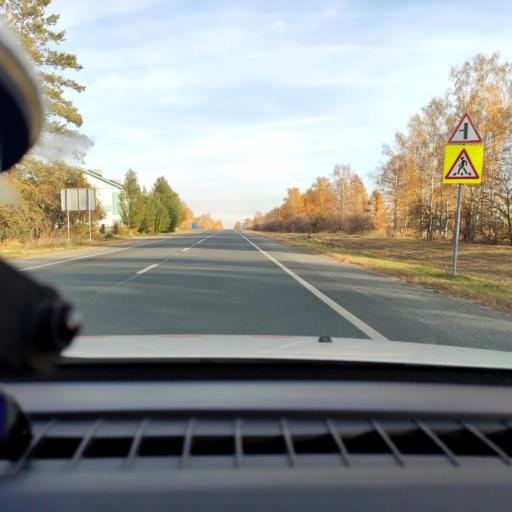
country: RU
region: Samara
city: Volzhskiy
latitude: 53.4538
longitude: 50.1262
